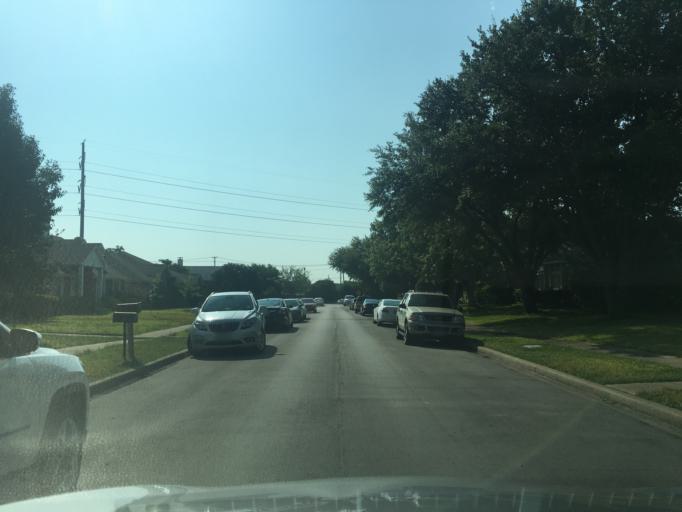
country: US
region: Texas
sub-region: Dallas County
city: Garland
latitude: 32.9412
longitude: -96.6246
